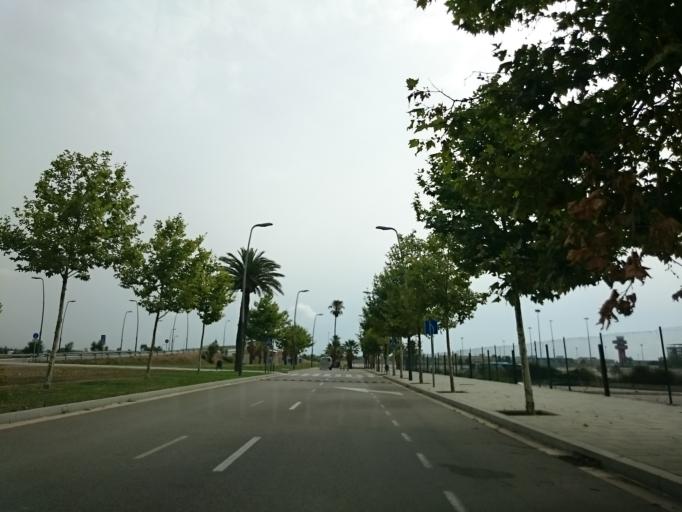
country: ES
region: Catalonia
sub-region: Provincia de Barcelona
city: El Prat de Llobregat
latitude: 41.3068
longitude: 2.0737
